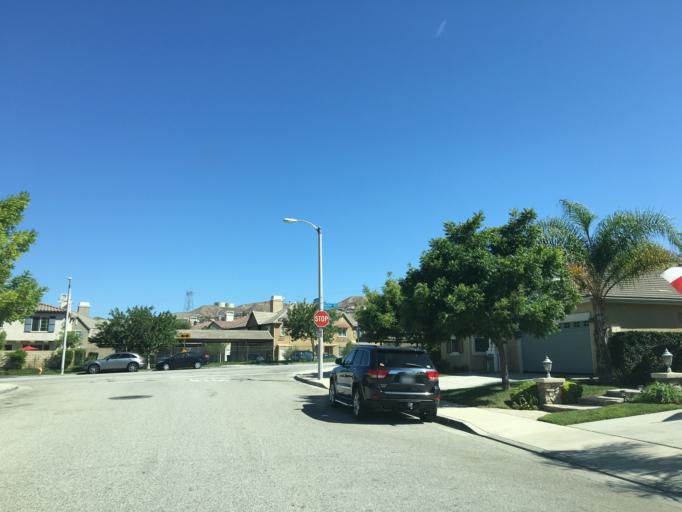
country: US
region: California
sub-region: Los Angeles County
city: Santa Clarita
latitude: 34.4437
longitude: -118.4735
